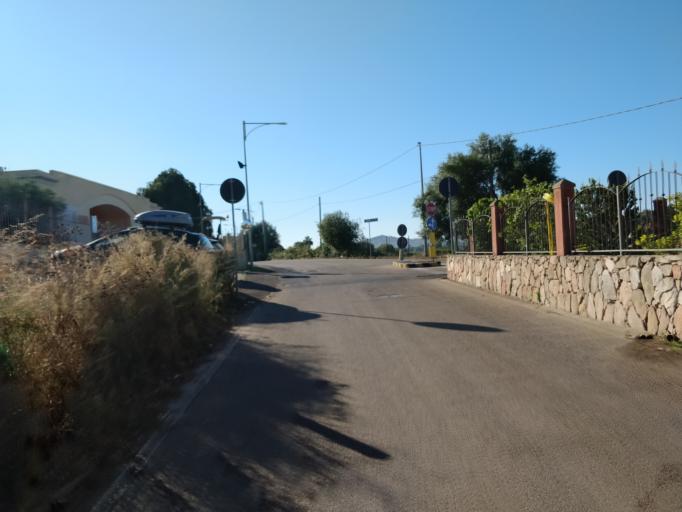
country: IT
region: Sardinia
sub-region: Provincia di Ogliastra
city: Girasole
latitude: 39.9527
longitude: 9.6649
